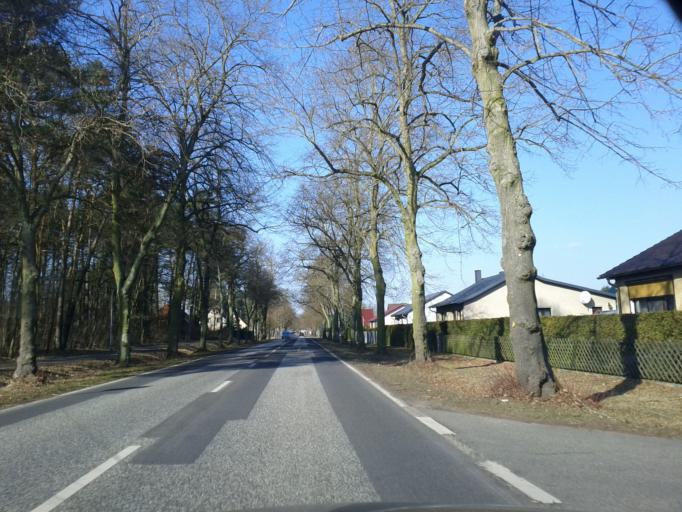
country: DE
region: Brandenburg
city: Spreenhagen
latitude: 52.3898
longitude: 13.9463
